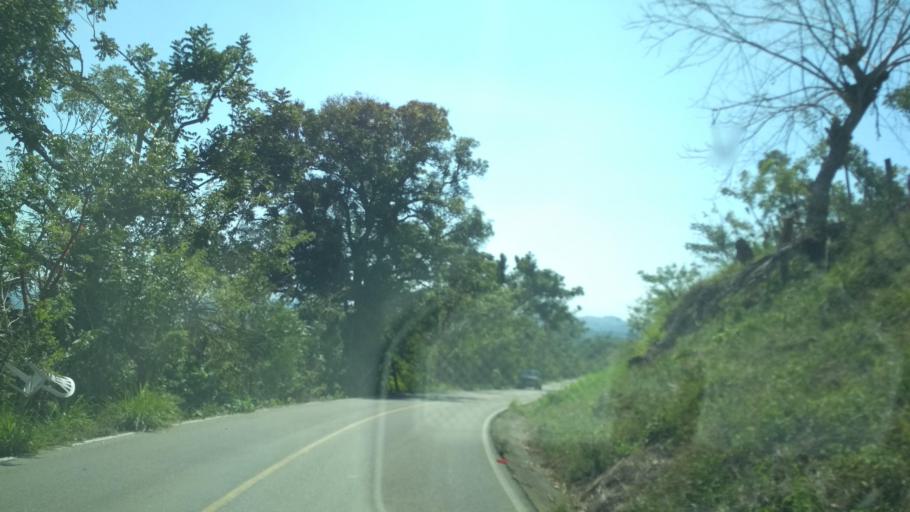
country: MX
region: Veracruz
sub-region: Papantla
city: Polutla
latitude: 20.4625
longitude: -97.2221
